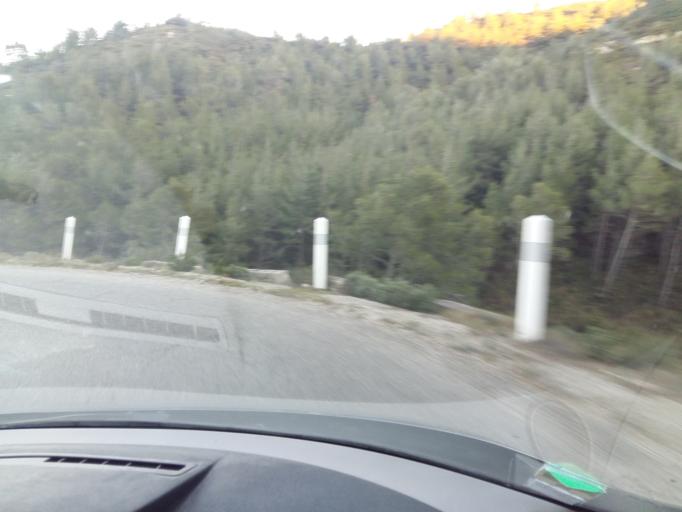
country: FR
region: Provence-Alpes-Cote d'Azur
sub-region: Departement des Bouches-du-Rhone
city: Maussane-les-Alpilles
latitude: 43.7577
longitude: 4.7939
